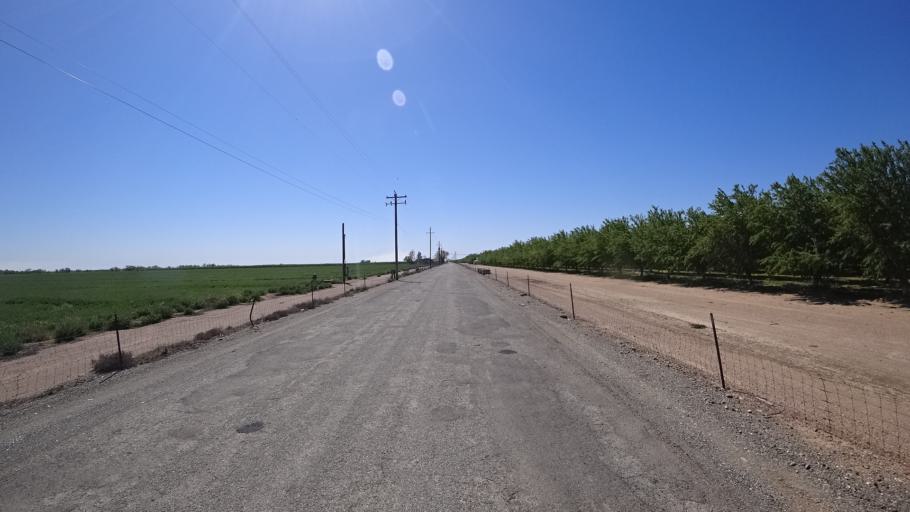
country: US
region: California
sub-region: Glenn County
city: Orland
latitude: 39.6676
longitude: -122.2346
